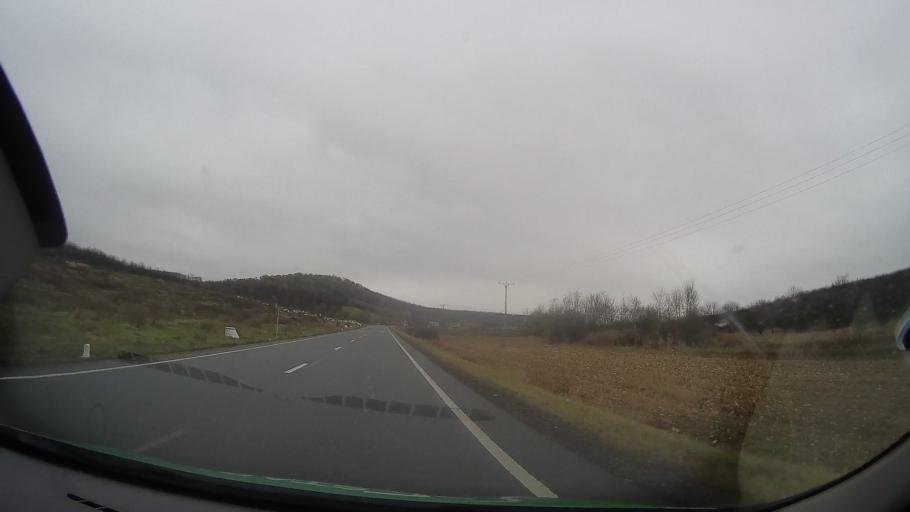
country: RO
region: Mures
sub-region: Comuna Breaza
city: Breaza
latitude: 46.7820
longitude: 24.6533
